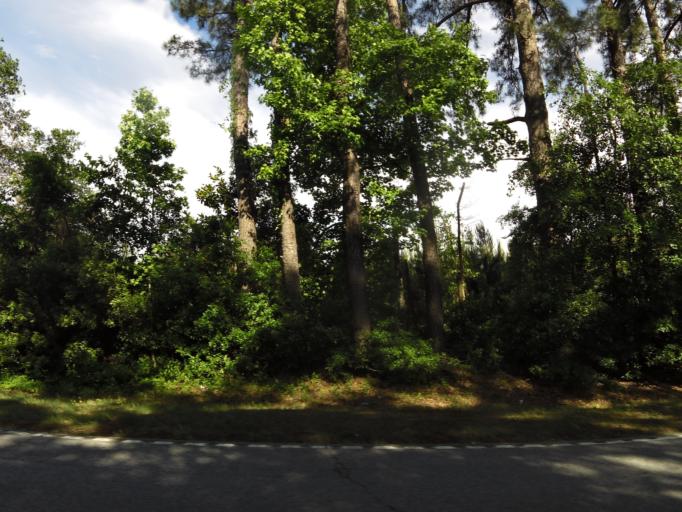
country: US
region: South Carolina
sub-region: Allendale County
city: Allendale
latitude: 33.0918
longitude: -81.2076
